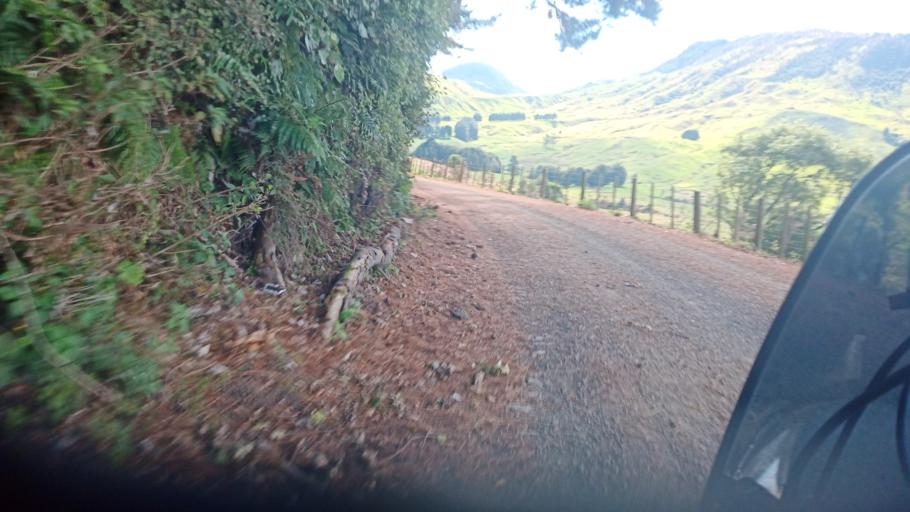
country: NZ
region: Bay of Plenty
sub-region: Opotiki District
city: Opotiki
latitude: -38.3522
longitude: 177.5873
